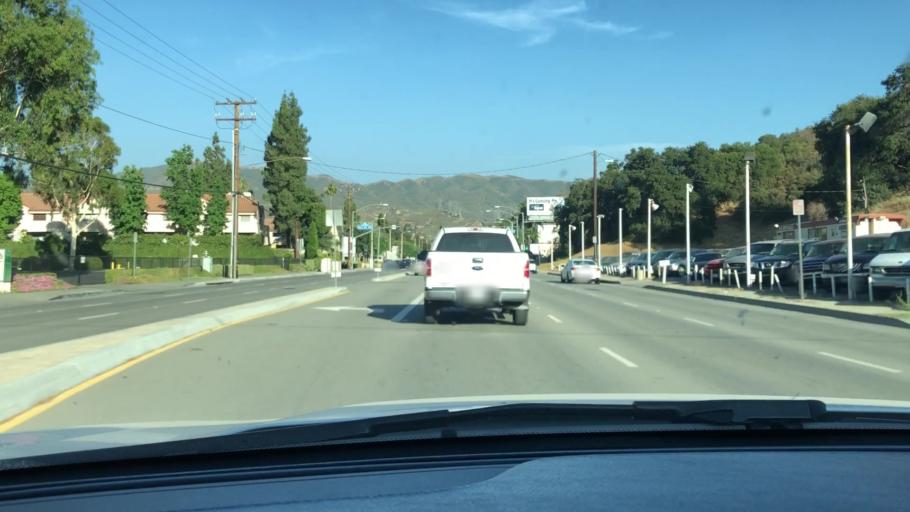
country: US
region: California
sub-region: Los Angeles County
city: Santa Clarita
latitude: 34.3716
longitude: -118.5160
